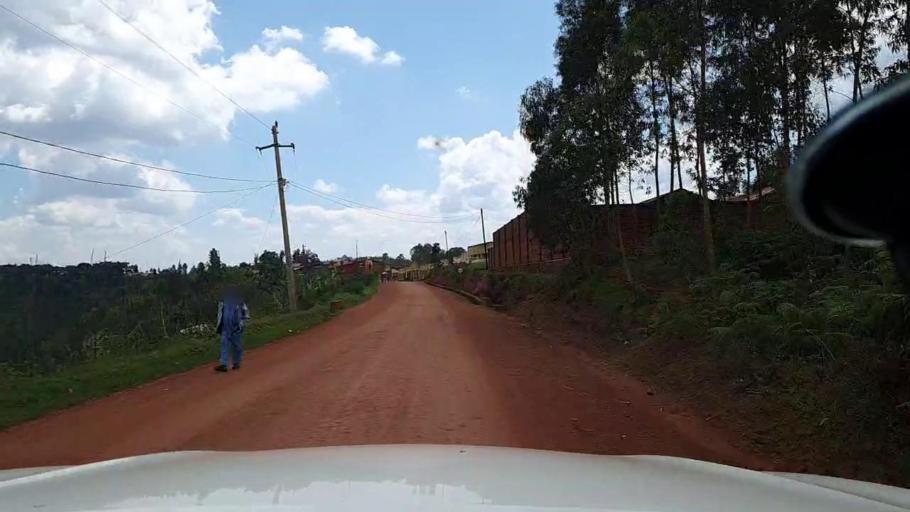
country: RW
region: Kigali
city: Kigali
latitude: -1.8027
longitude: 29.8423
